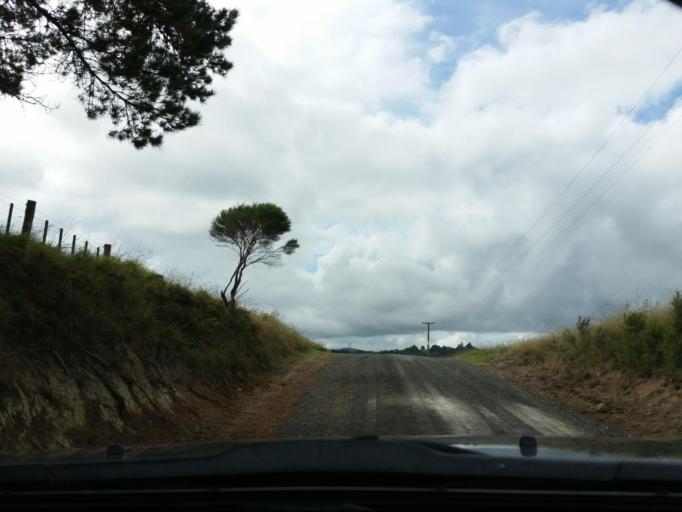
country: NZ
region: Northland
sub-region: Whangarei
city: Maungatapere
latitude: -35.8050
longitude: 174.0467
